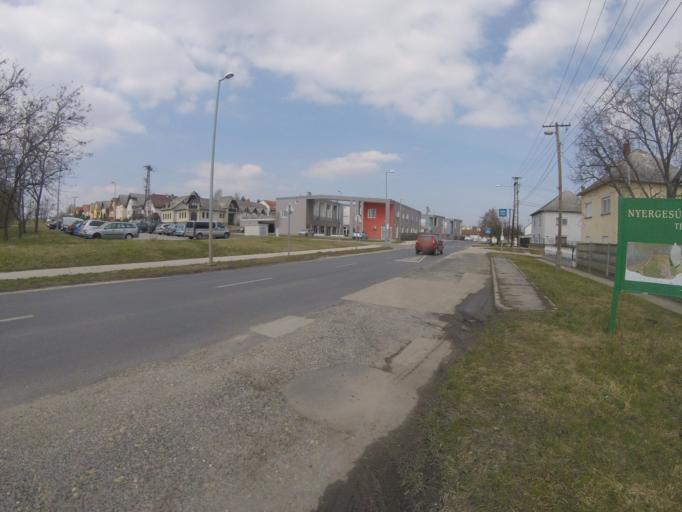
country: HU
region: Komarom-Esztergom
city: Nyergesujfalu
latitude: 47.7555
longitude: 18.5550
